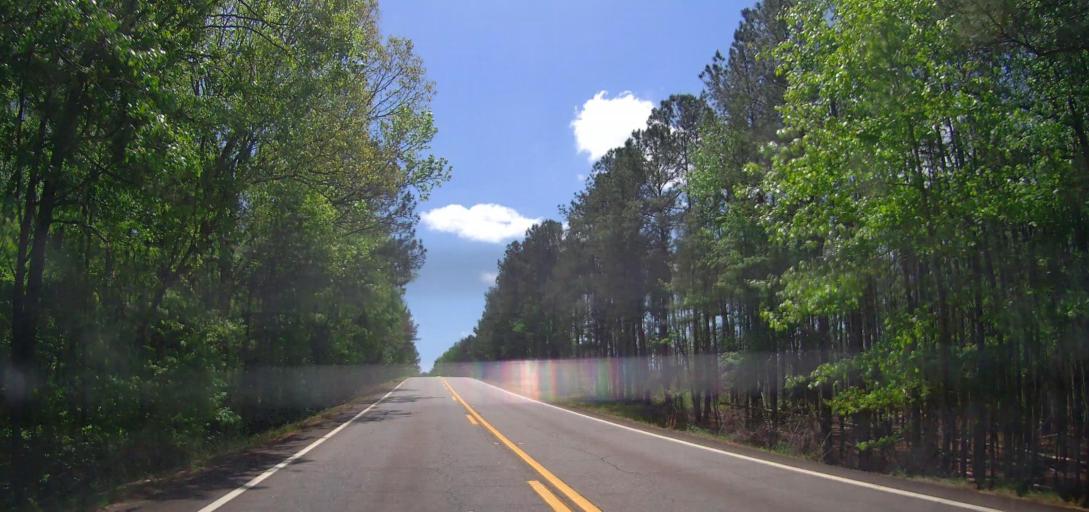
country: US
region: Georgia
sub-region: Jones County
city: Gray
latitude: 33.1278
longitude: -83.6292
